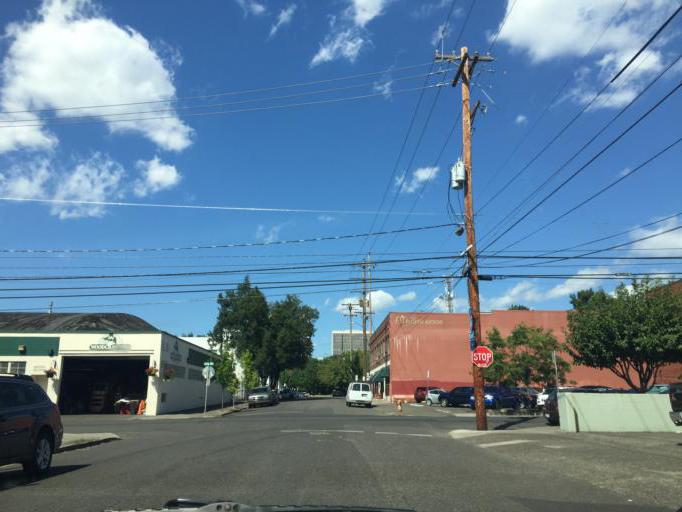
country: US
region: Oregon
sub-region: Multnomah County
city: Portland
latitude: 45.5241
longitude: -122.6587
